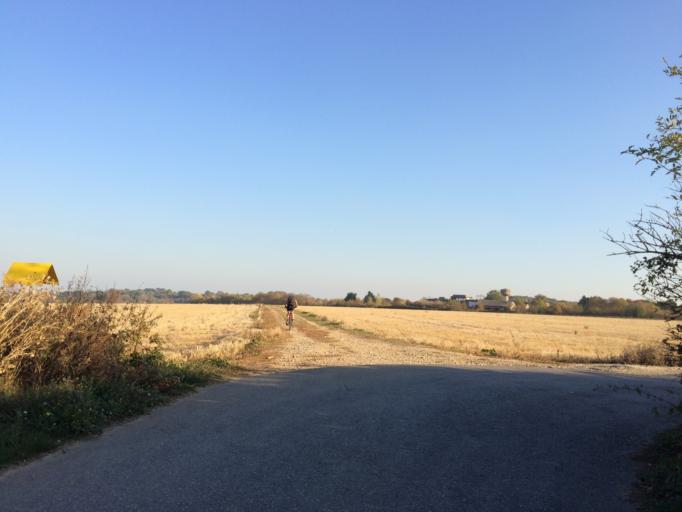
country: FR
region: Ile-de-France
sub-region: Departement de l'Essonne
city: Nozay
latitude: 48.6700
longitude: 2.2416
